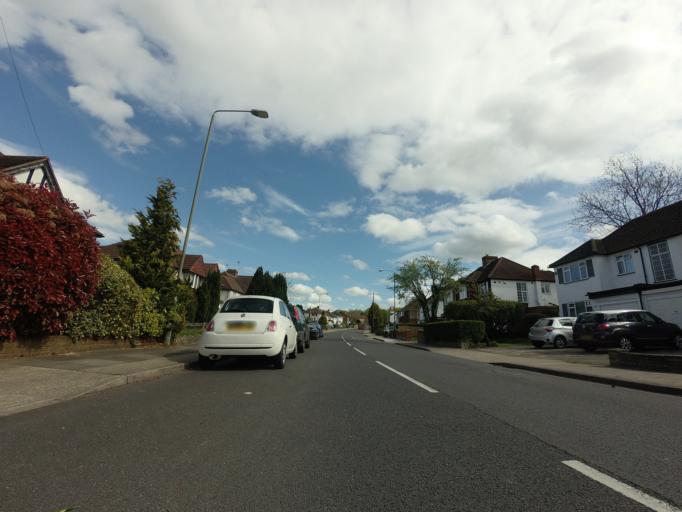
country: GB
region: England
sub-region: Greater London
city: Orpington
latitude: 51.3716
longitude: 0.1126
